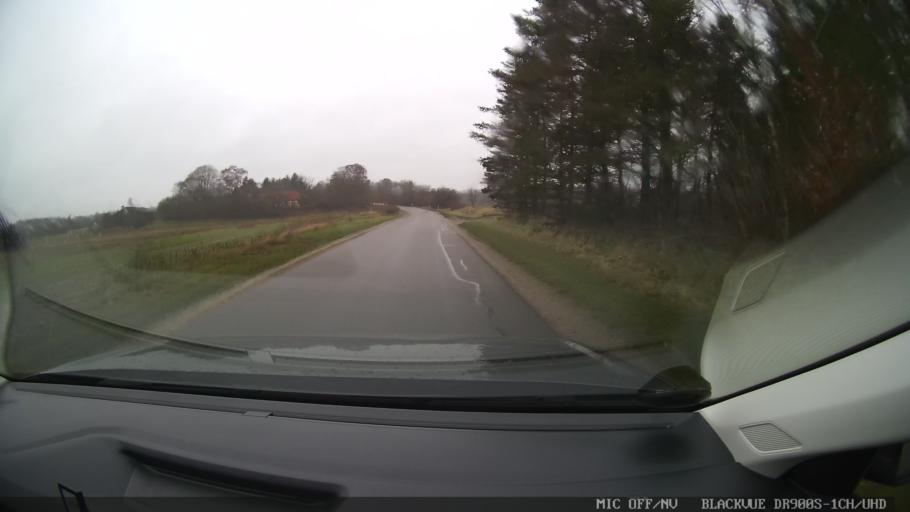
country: DK
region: Central Jutland
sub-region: Viborg Kommune
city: Karup
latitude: 56.2885
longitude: 9.1653
